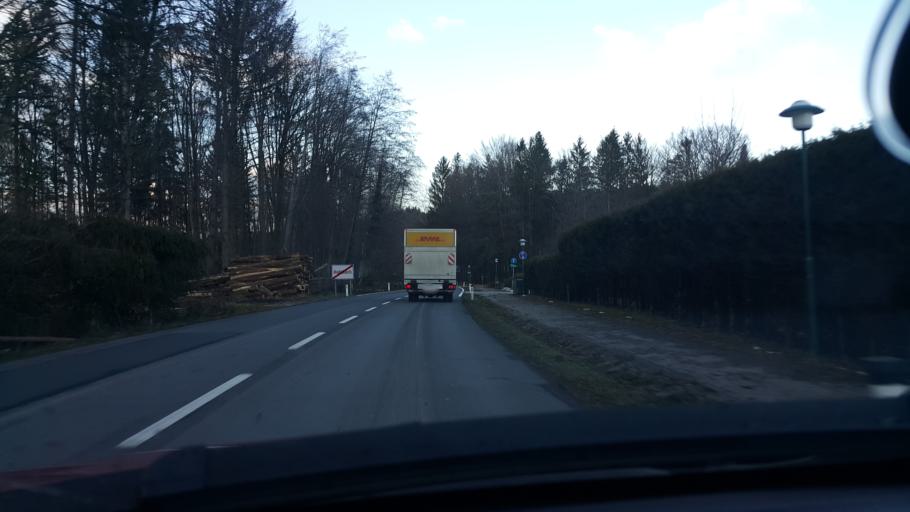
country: AT
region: Styria
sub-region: Politischer Bezirk Deutschlandsberg
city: Hollenegg
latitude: 46.7886
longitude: 15.2369
